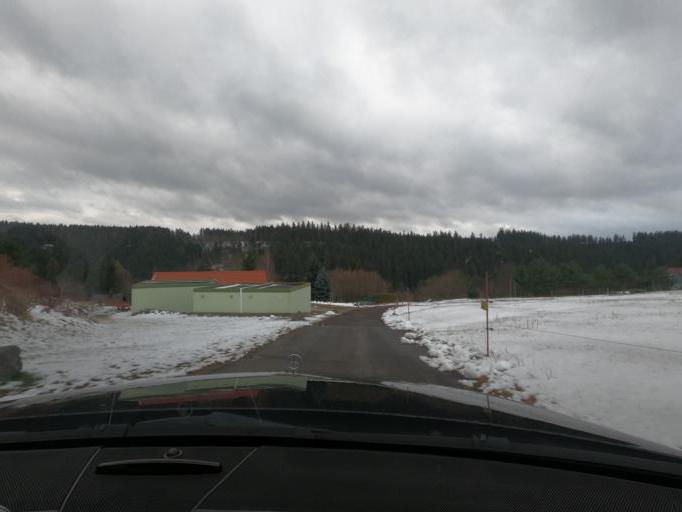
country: DE
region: Thuringia
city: Finsterbergen
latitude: 50.8322
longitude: 10.5954
